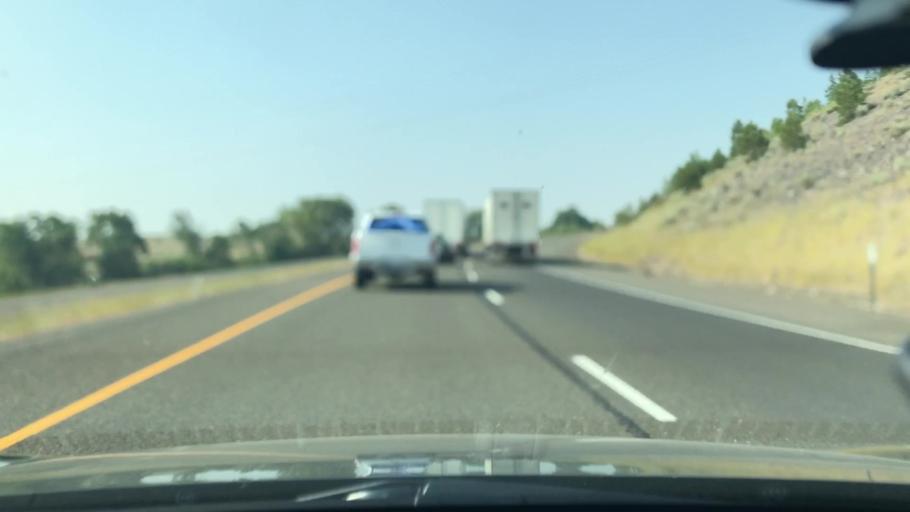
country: US
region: Oregon
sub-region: Union County
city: Union
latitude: 45.1504
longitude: -117.9718
